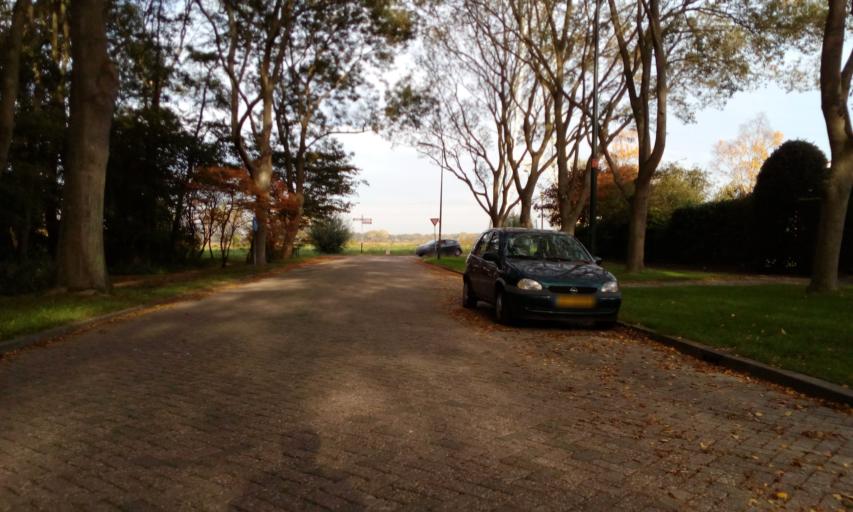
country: NL
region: South Holland
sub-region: Gemeente Leidschendam-Voorburg
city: Voorburg
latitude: 52.0941
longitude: 4.3802
